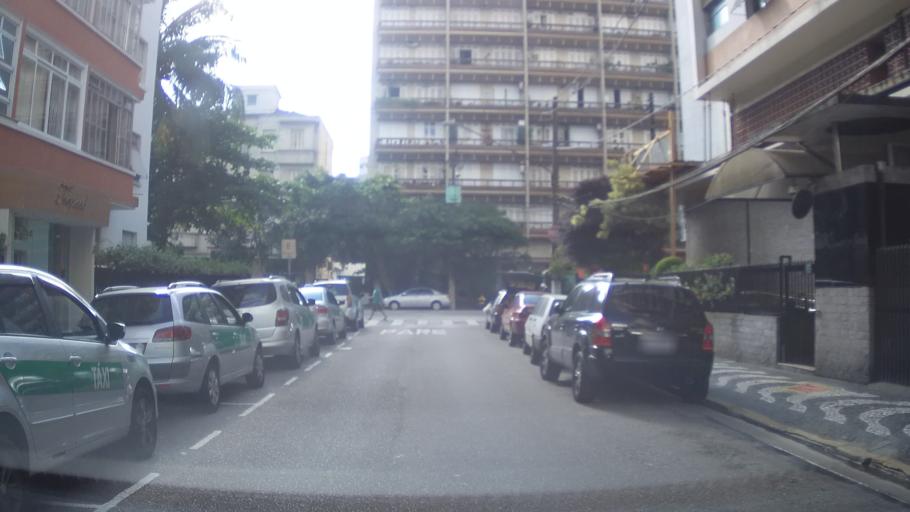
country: BR
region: Sao Paulo
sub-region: Santos
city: Santos
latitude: -23.9711
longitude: -46.3246
